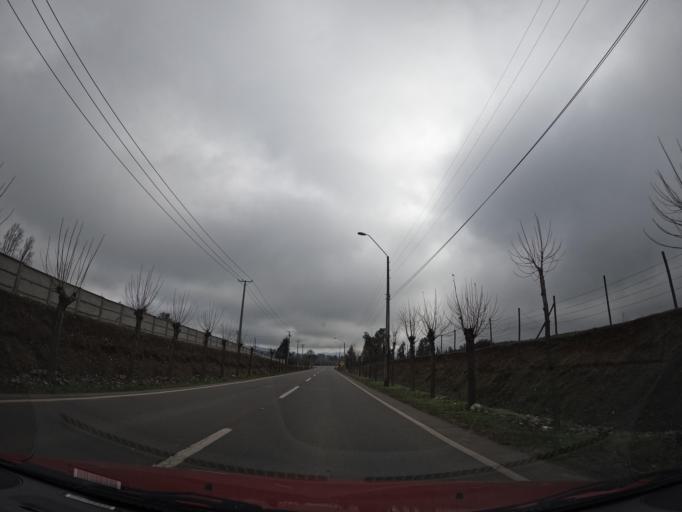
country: CL
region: Maule
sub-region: Provincia de Cauquenes
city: Cauquenes
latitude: -36.2718
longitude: -72.5443
